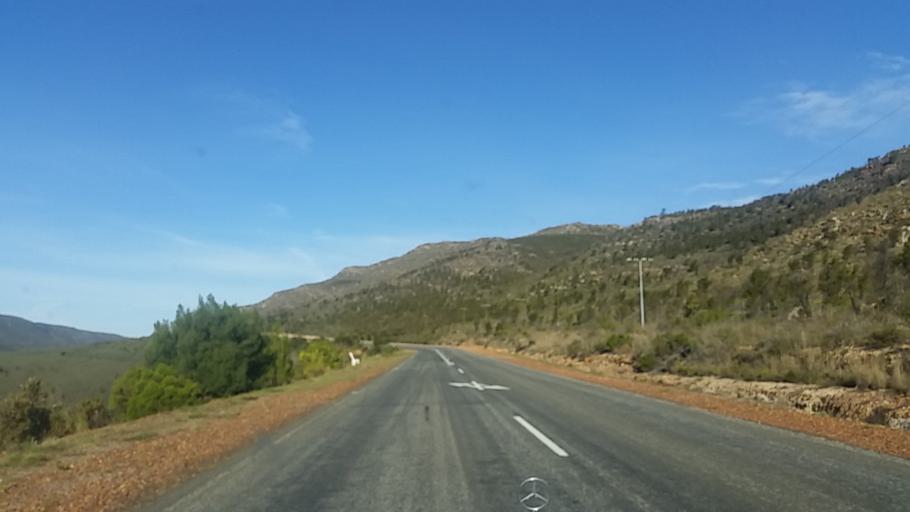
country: ZA
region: Western Cape
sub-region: Eden District Municipality
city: Knysna
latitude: -33.7522
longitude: 22.9541
